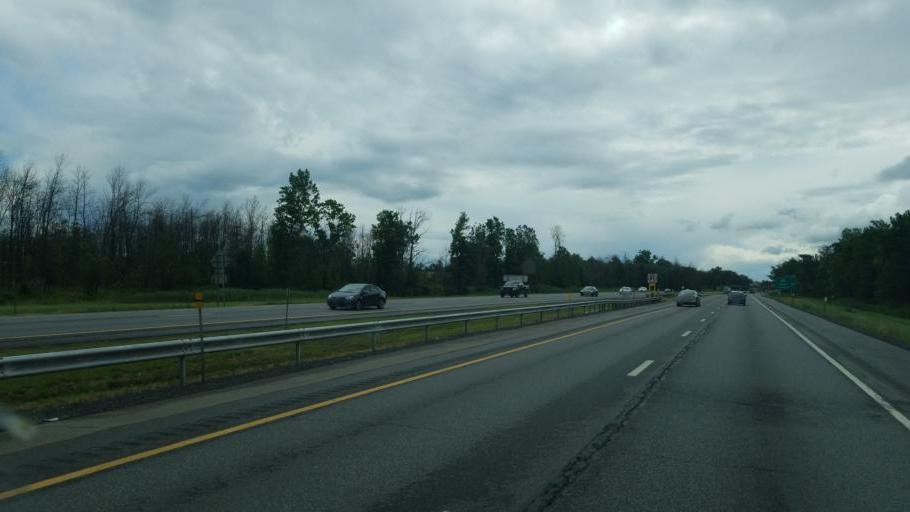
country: US
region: New York
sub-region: Erie County
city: Williamsville
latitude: 42.9507
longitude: -78.7133
